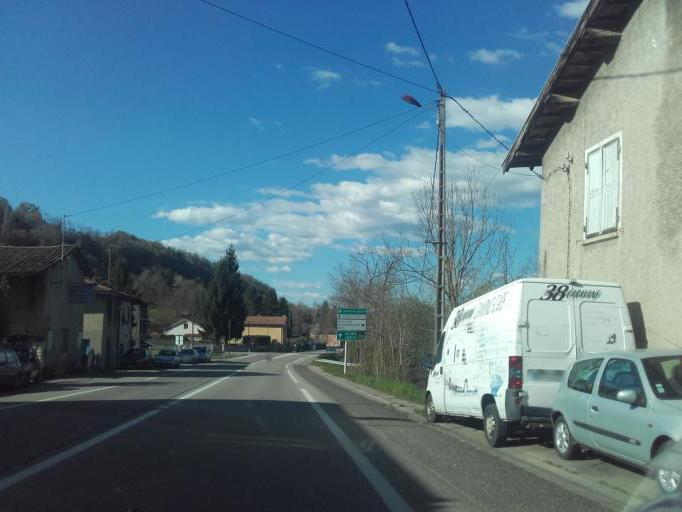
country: FR
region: Rhone-Alpes
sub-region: Departement de l'Isere
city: Nivolas-Vermelle
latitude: 45.5368
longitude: 5.3101
